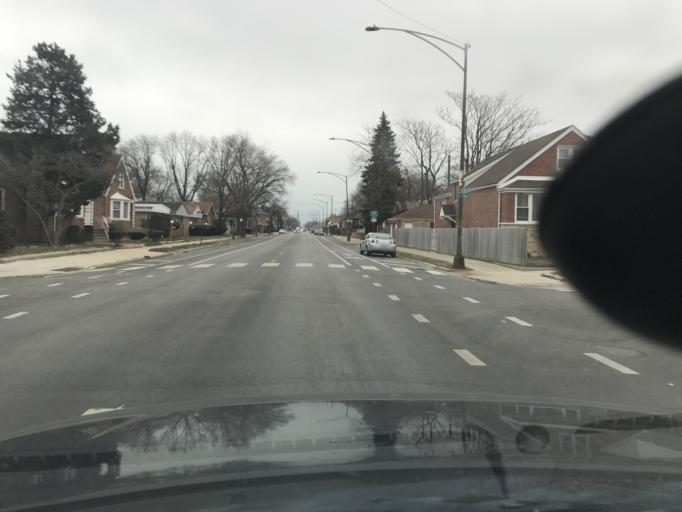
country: US
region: Indiana
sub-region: Lake County
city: Whiting
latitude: 41.7444
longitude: -87.5712
